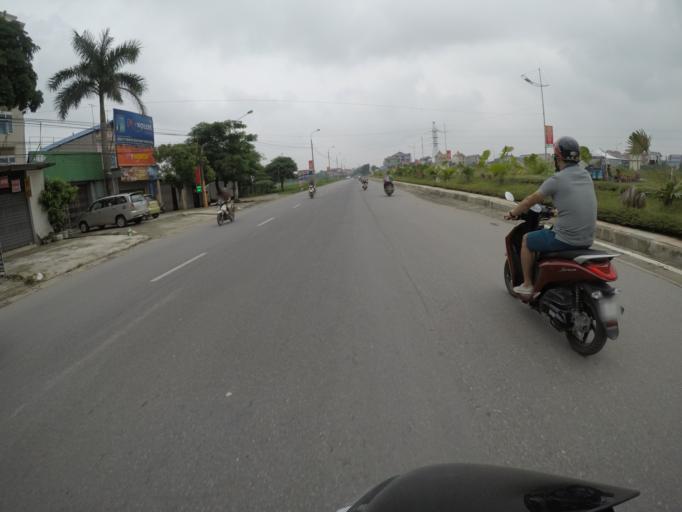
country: VN
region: Ha Noi
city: Soc Son
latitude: 21.2627
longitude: 105.8507
